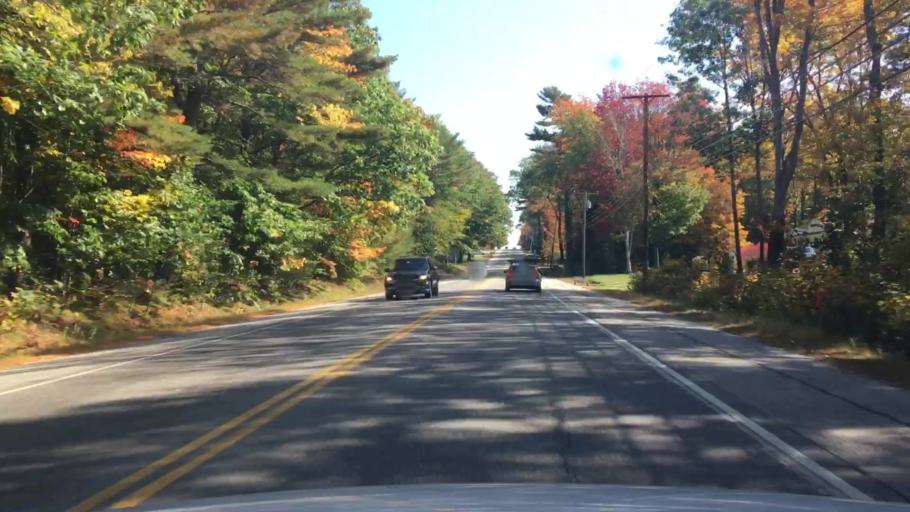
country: US
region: Maine
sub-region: Sagadahoc County
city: Topsham
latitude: 43.9506
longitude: -69.9930
